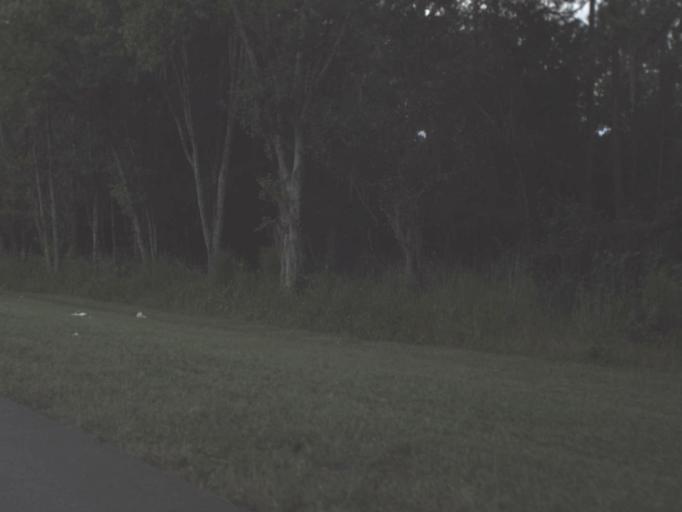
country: US
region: Florida
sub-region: Polk County
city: Kathleen
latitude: 28.1989
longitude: -82.0040
